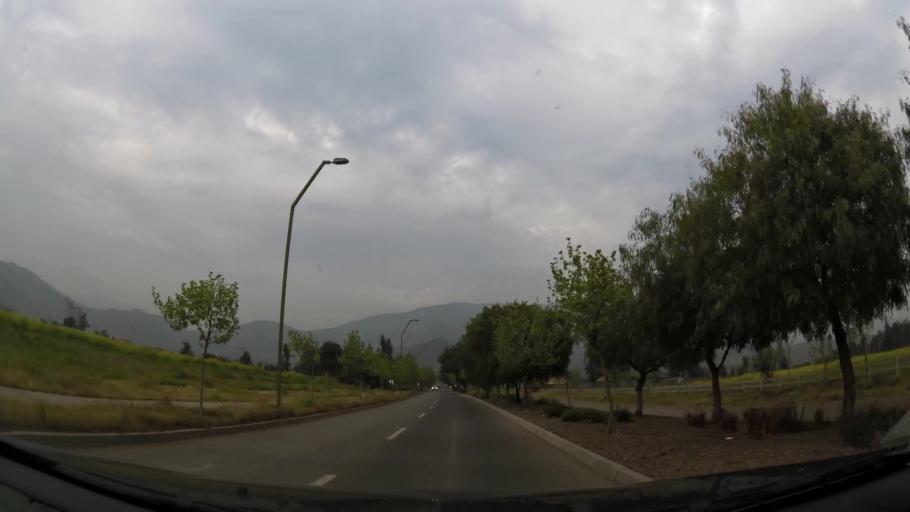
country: CL
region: Santiago Metropolitan
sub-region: Provincia de Chacabuco
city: Chicureo Abajo
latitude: -33.2012
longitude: -70.6561
